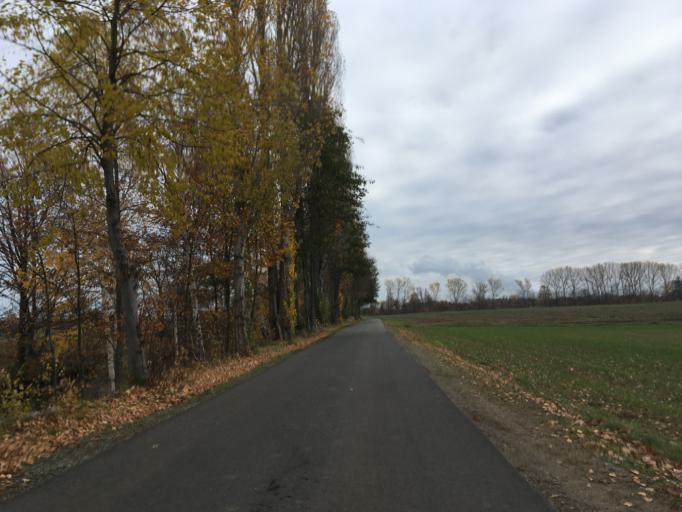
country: DE
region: Brandenburg
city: Drehnow
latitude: 51.8619
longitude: 14.3565
